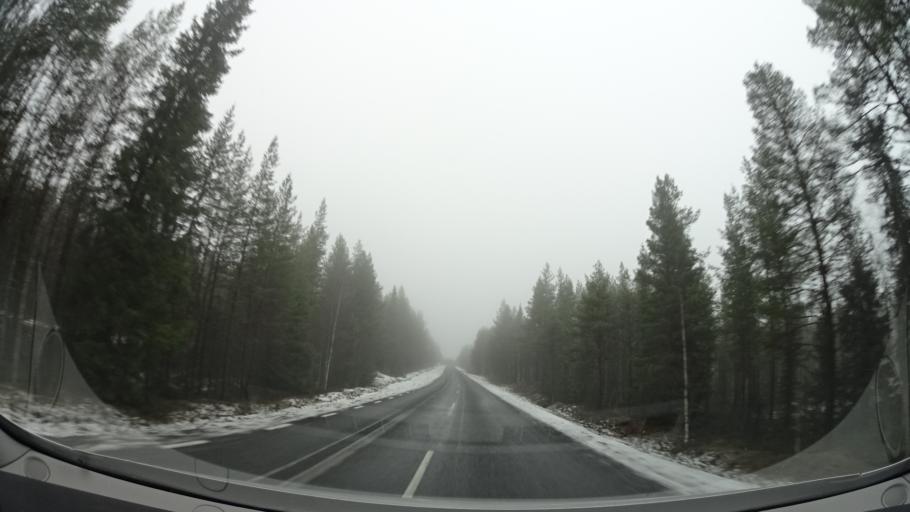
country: SE
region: Vaesterbotten
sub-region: Asele Kommun
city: Insjon
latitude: 64.2370
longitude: 17.5505
